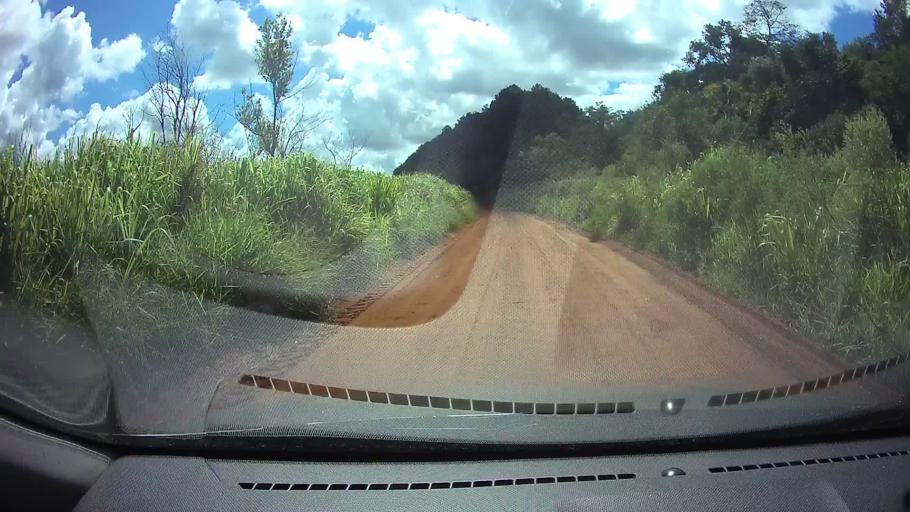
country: PY
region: Paraguari
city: La Colmena
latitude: -25.9540
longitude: -56.7702
